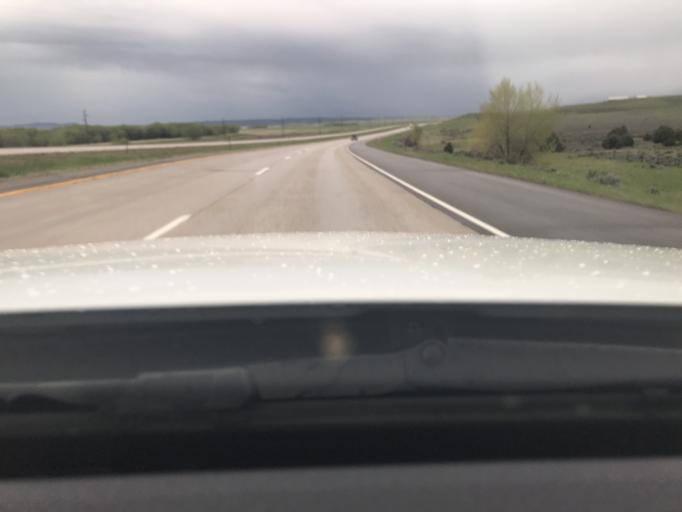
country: US
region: Wyoming
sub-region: Converse County
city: Douglas
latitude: 42.5602
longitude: -105.0468
